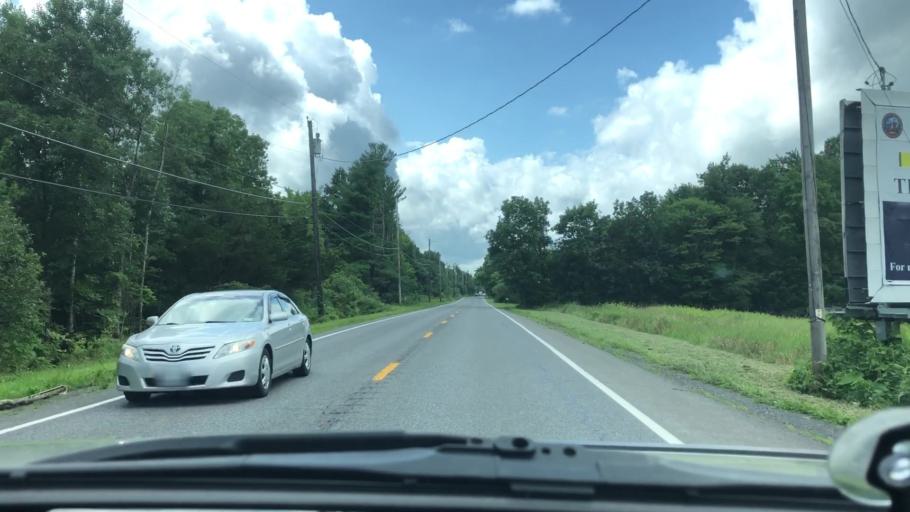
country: US
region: New York
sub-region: Greene County
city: Palenville
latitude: 42.1535
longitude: -73.9992
